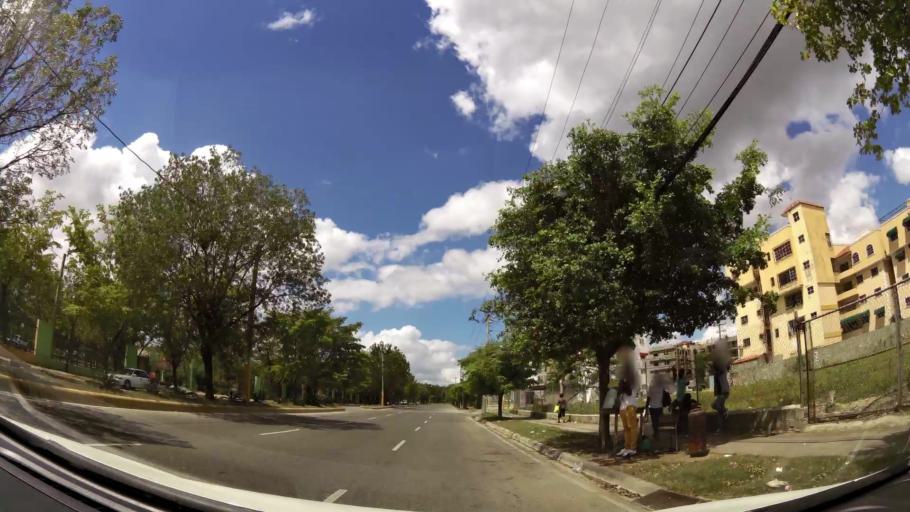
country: DO
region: Nacional
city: La Agustina
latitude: 18.5184
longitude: -69.9172
